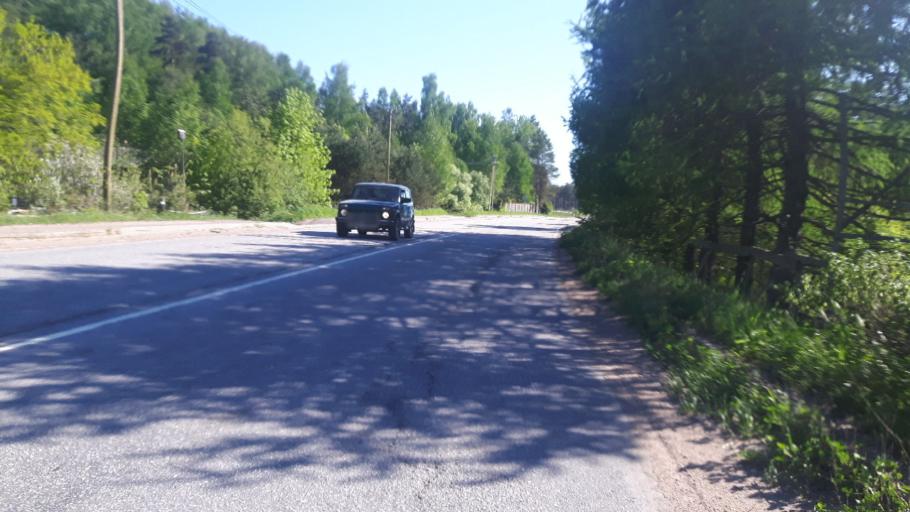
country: RU
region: Leningrad
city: Sosnovyy Bor
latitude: 60.2093
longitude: 29.0063
